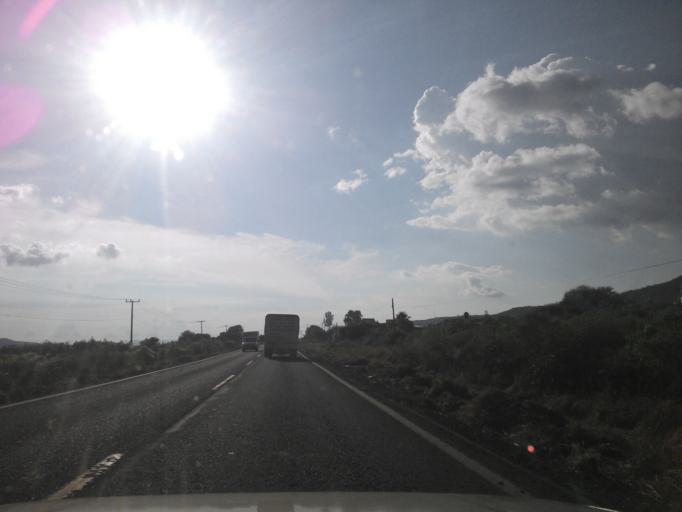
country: MX
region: Jalisco
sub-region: Atotonilco el Alto
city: Vistas del Maguey [Fraccionamiento]
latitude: 20.5414
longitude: -102.5751
